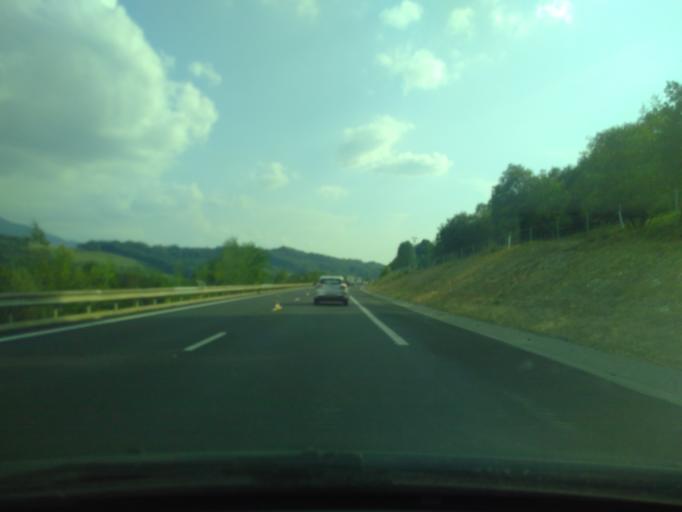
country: FR
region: Rhone-Alpes
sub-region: Departement de la Haute-Savoie
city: Evires
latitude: 46.0315
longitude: 6.2338
